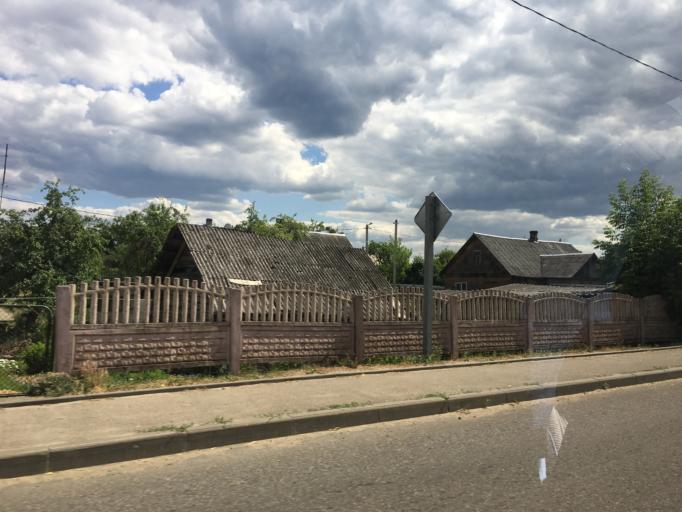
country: LT
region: Alytaus apskritis
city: Druskininkai
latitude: 53.8848
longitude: 24.1345
